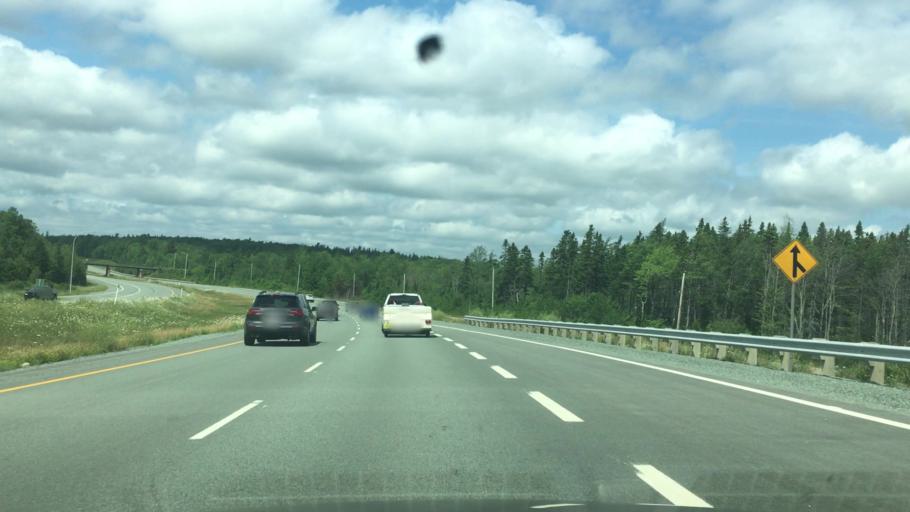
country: CA
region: Nova Scotia
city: Oxford
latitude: 45.6957
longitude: -63.7777
